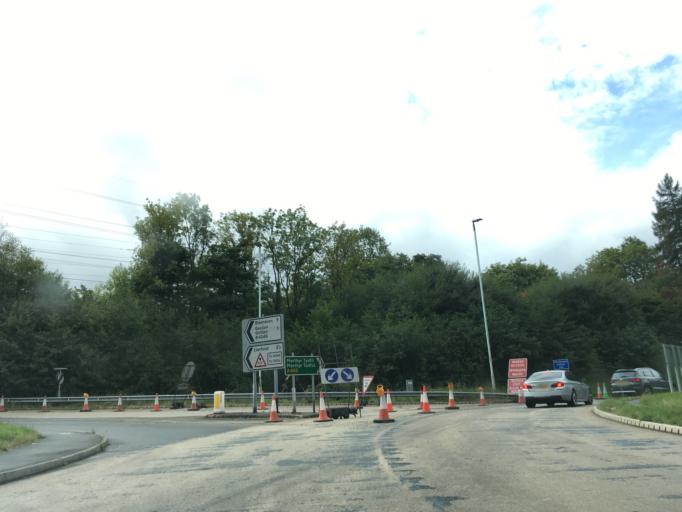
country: GB
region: Wales
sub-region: Monmouthshire
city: Gilwern
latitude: 51.8224
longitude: -3.0758
